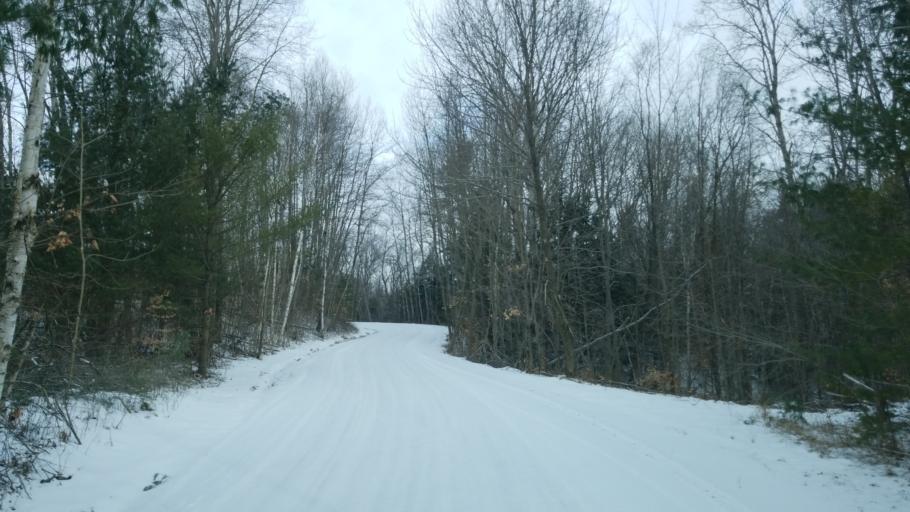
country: US
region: Michigan
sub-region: Osceola County
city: Evart
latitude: 43.8119
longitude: -85.2674
